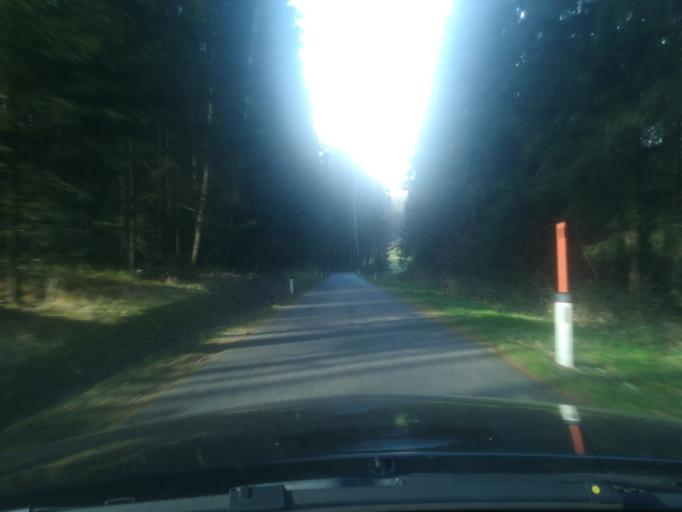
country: AT
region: Upper Austria
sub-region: Politischer Bezirk Perg
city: Perg
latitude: 48.3213
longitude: 14.6614
